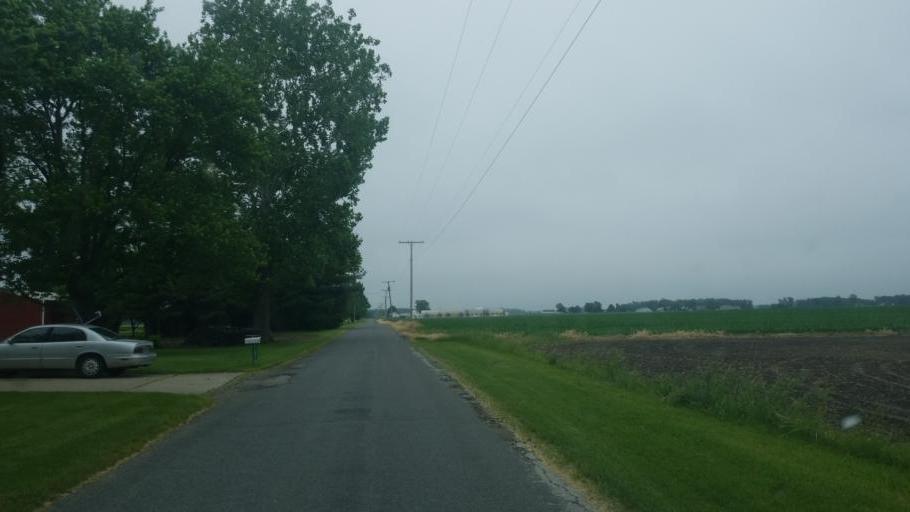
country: US
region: Indiana
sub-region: Marshall County
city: Bremen
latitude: 41.5079
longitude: -86.1328
